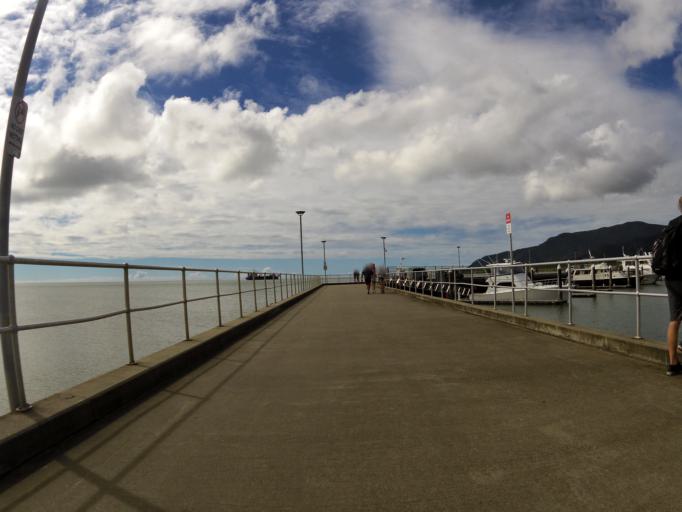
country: AU
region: Queensland
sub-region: Cairns
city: Cairns
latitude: -16.9175
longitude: 145.7809
